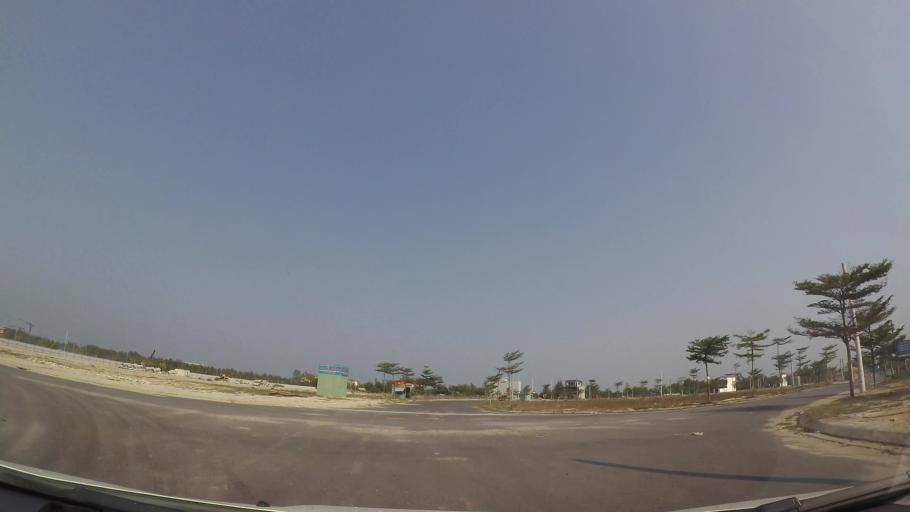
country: VN
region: Da Nang
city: Ngu Hanh Son
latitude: 15.9568
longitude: 108.2747
